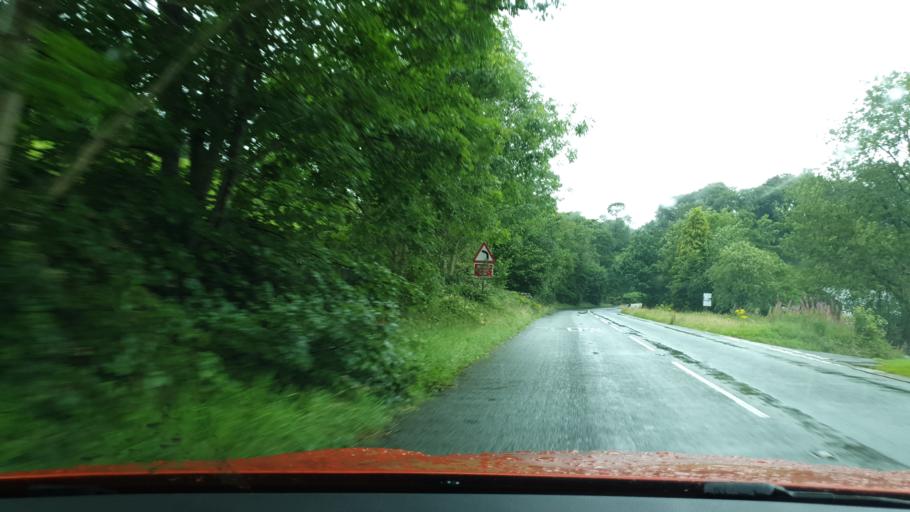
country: GB
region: England
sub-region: Cumbria
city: Ulverston
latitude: 54.3217
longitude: -3.0933
